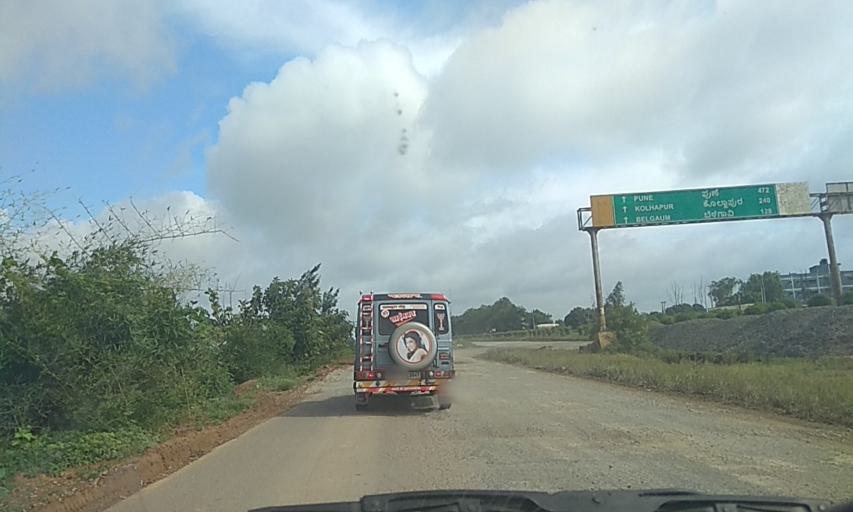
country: IN
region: Karnataka
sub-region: Haveri
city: Shiggaon
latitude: 15.0432
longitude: 75.1710
